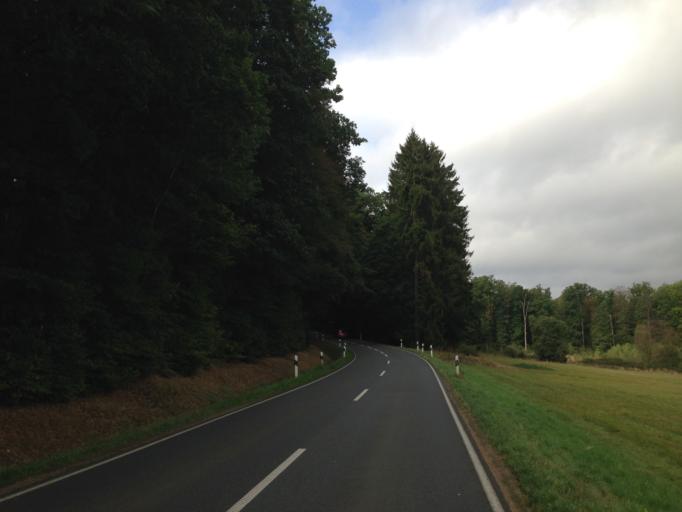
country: DE
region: Hesse
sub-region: Regierungsbezirk Giessen
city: Bad Endbach
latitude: 50.6730
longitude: 8.5548
